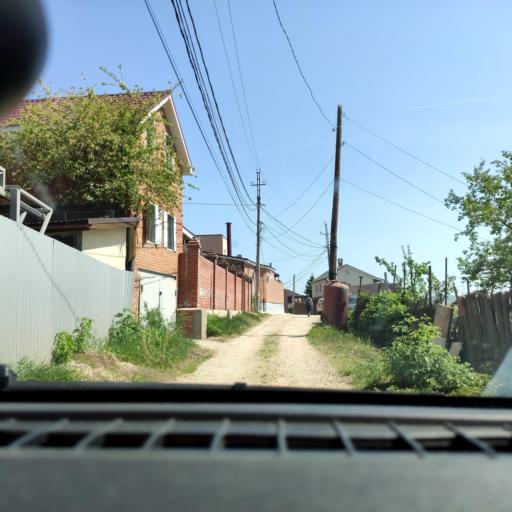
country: RU
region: Samara
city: Tol'yatti
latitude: 53.4742
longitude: 49.3661
